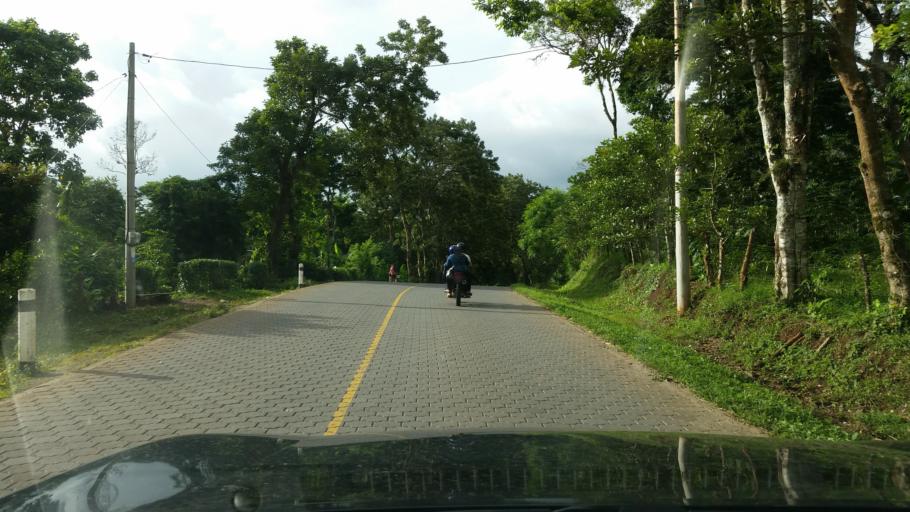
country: NI
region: Matagalpa
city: San Ramon
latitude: 13.1683
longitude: -85.7276
